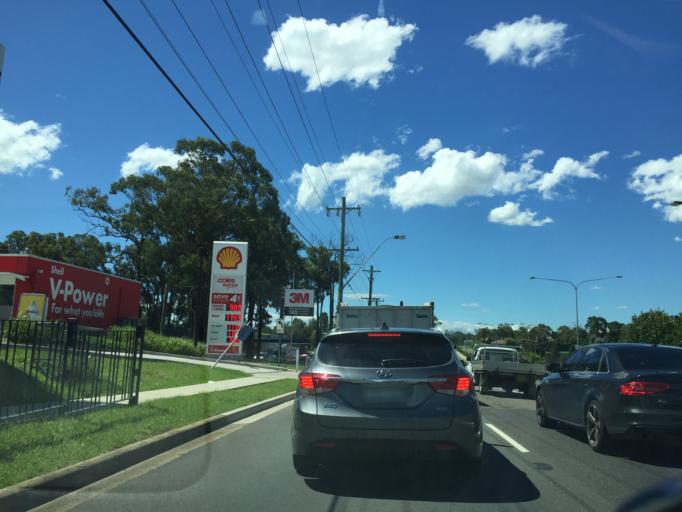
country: AU
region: New South Wales
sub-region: Blacktown
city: Blacktown
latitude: -33.7541
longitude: 150.9150
